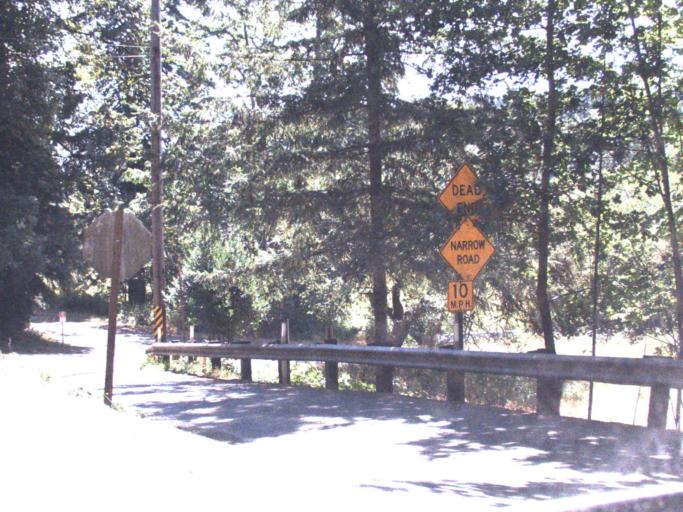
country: US
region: Washington
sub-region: King County
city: Ames Lake
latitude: 47.6279
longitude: -121.9870
